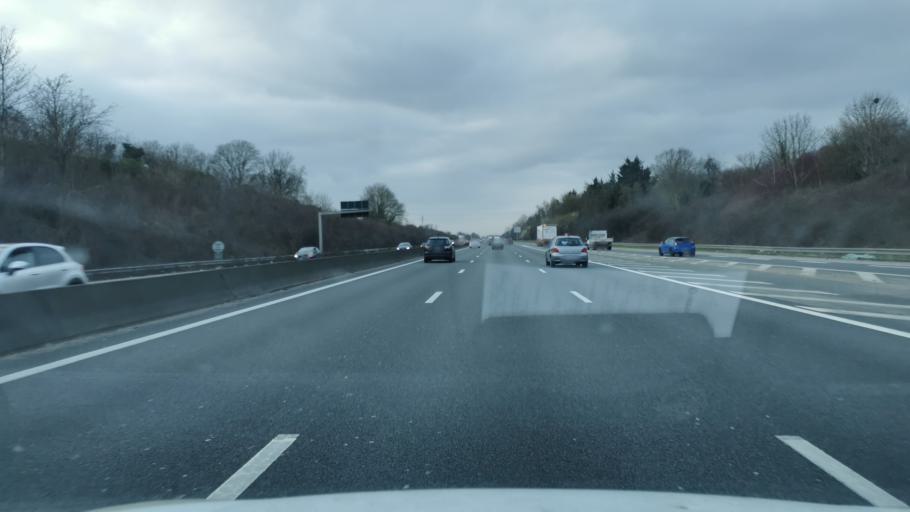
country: FR
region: Ile-de-France
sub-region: Departement du Val-d'Oise
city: Herblay
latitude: 48.9987
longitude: 2.1770
